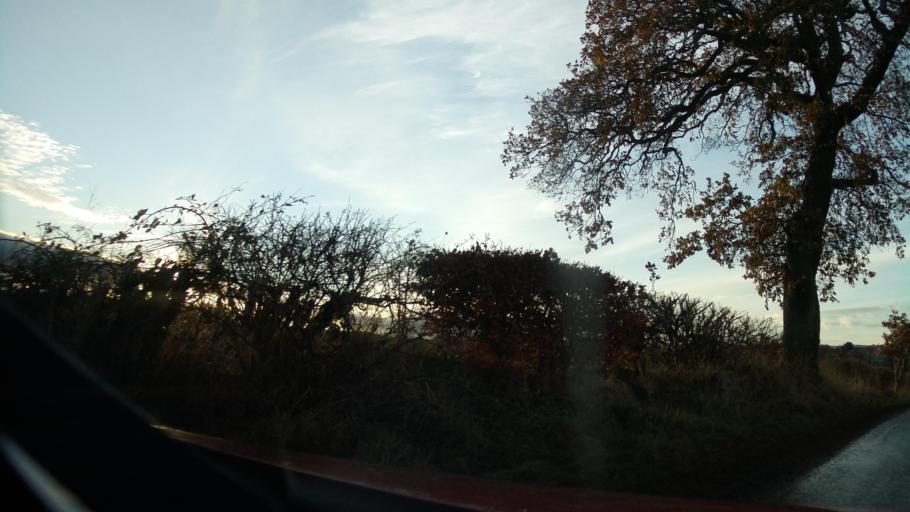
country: GB
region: Scotland
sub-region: Angus
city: Forfar
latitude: 56.5869
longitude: -2.8696
